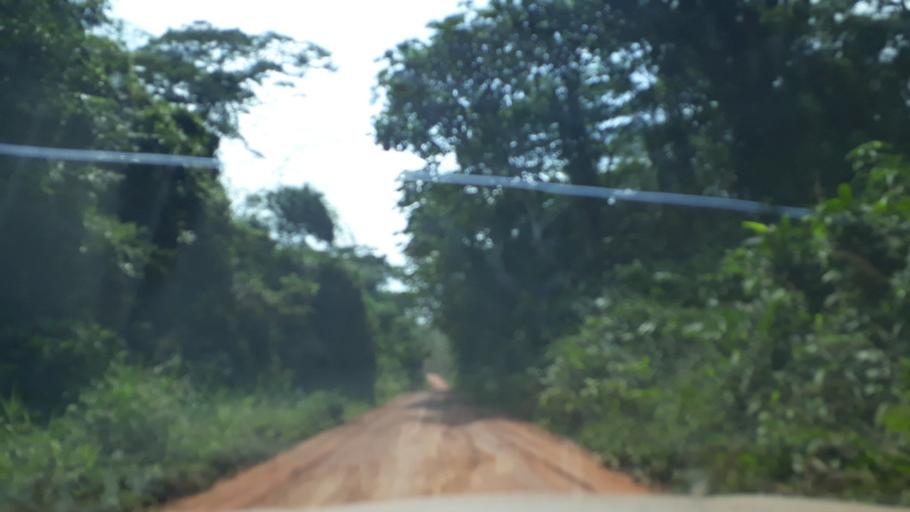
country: CD
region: Eastern Province
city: Wamba
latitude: 1.4303
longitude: 28.2047
